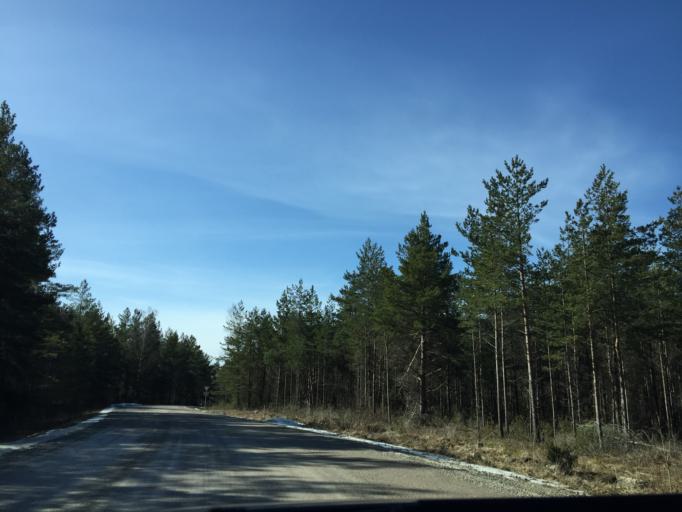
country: EE
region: Laeaene
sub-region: Lihula vald
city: Lihula
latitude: 58.6111
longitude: 23.5694
